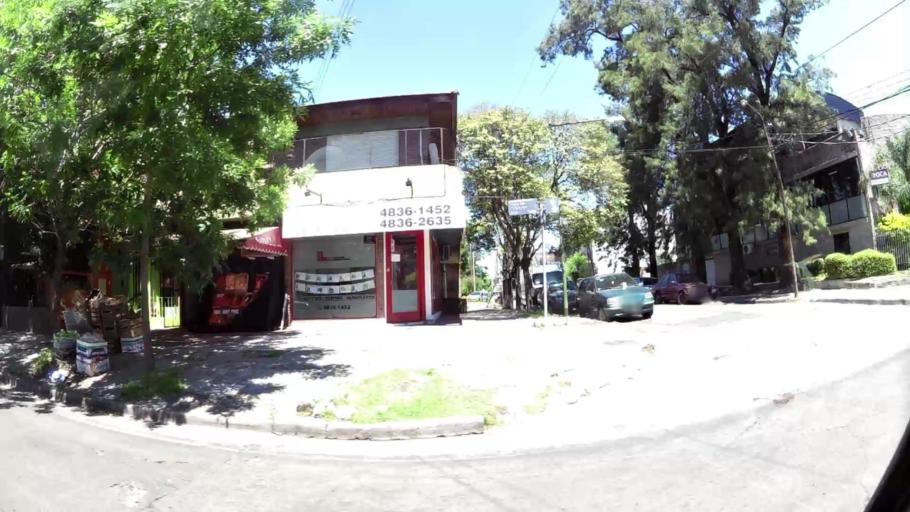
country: AR
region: Buenos Aires
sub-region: Partido de San Isidro
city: San Isidro
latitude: -34.4993
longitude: -58.5216
